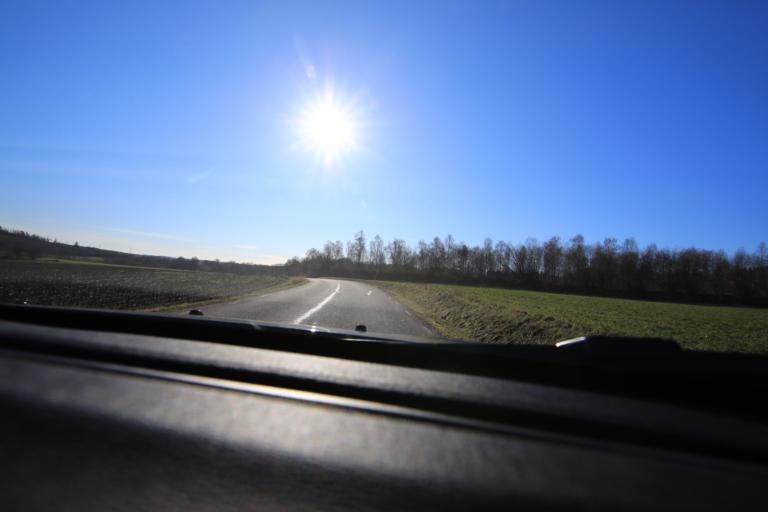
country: SE
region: Halland
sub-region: Varbergs Kommun
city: Tvaaker
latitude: 57.0653
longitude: 12.4632
